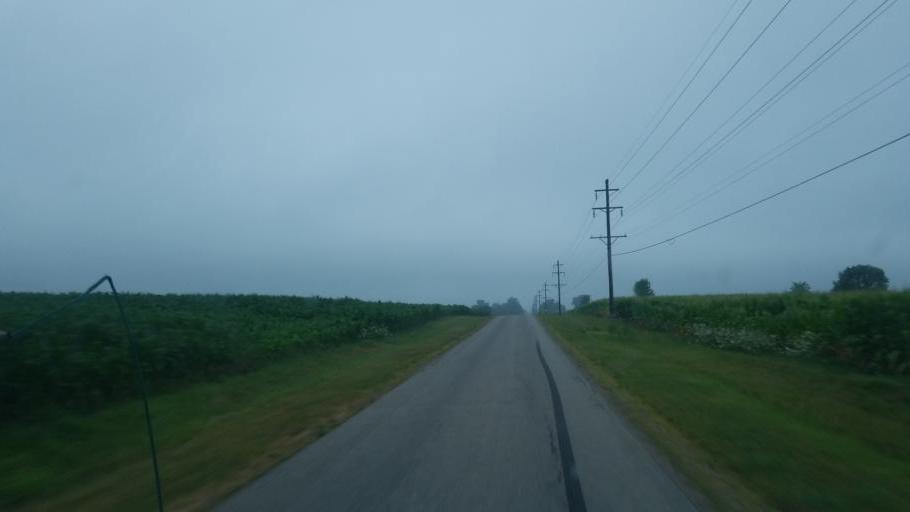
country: US
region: Ohio
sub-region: Defiance County
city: Hicksville
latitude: 41.3539
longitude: -84.7180
